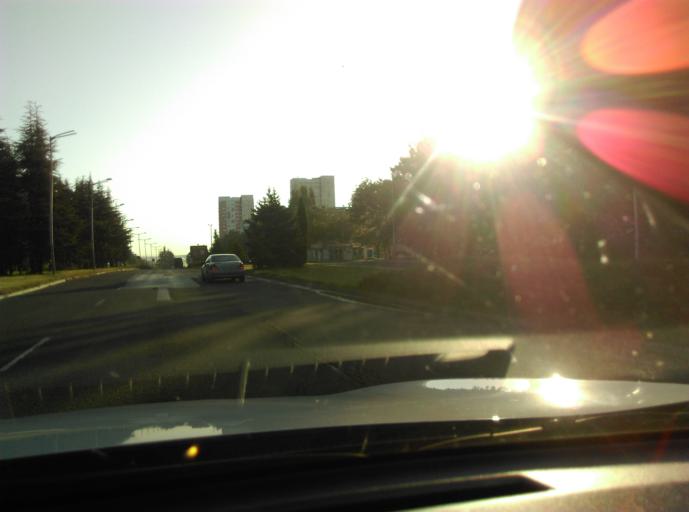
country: BG
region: Burgas
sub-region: Obshtina Burgas
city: Burgas
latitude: 42.5241
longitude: 27.4467
